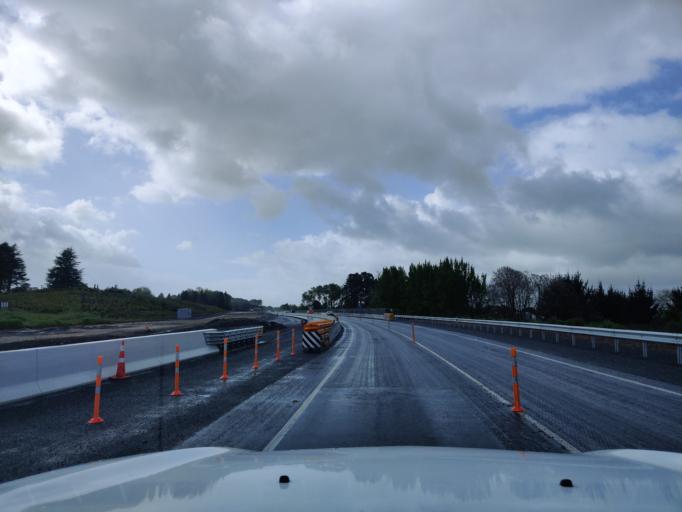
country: NZ
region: Waikato
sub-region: Hamilton City
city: Hamilton
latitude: -37.8178
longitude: 175.3433
